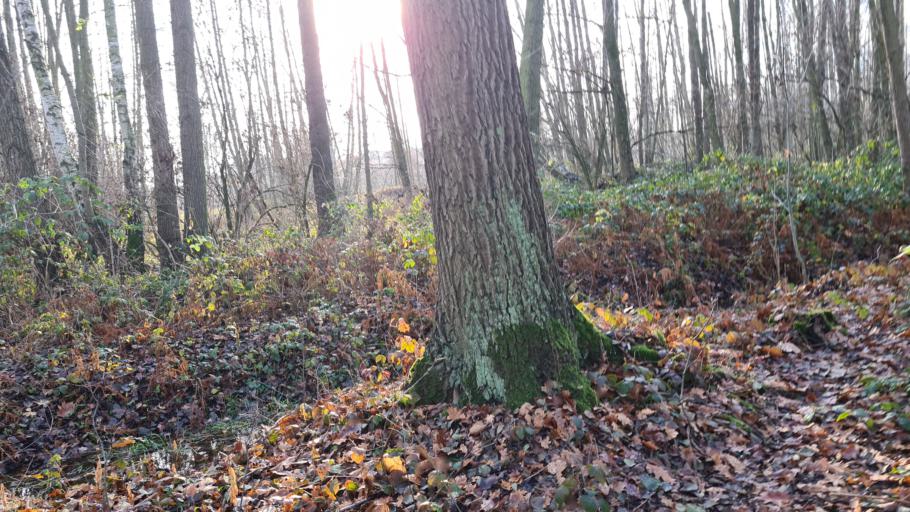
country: DE
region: Brandenburg
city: Doberlug-Kirchhain
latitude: 51.6318
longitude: 13.5809
